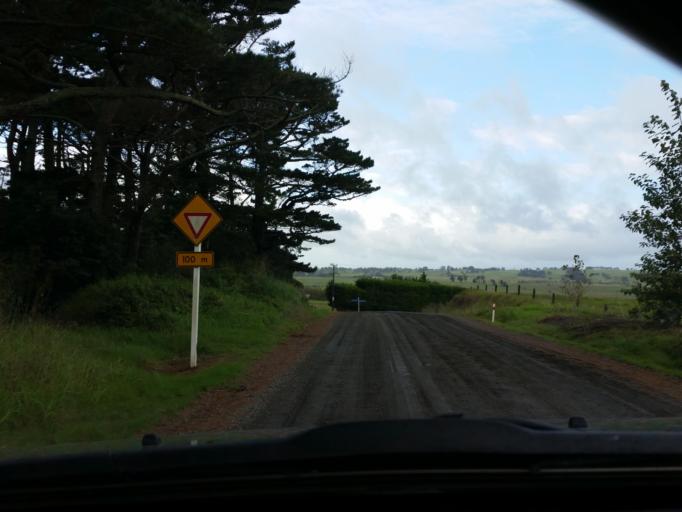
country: NZ
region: Northland
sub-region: Kaipara District
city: Dargaville
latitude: -36.0307
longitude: 173.8937
